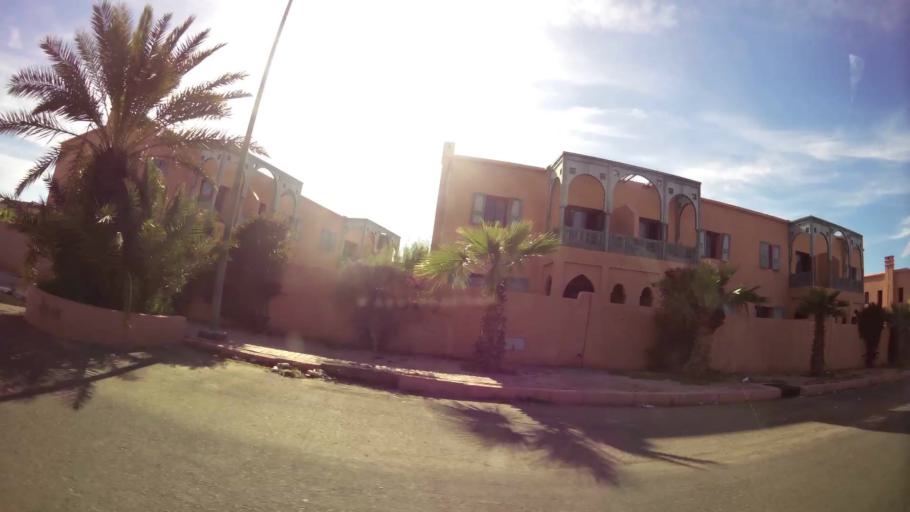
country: MA
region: Marrakech-Tensift-Al Haouz
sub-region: Marrakech
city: Marrakesh
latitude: 31.6739
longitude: -8.0517
